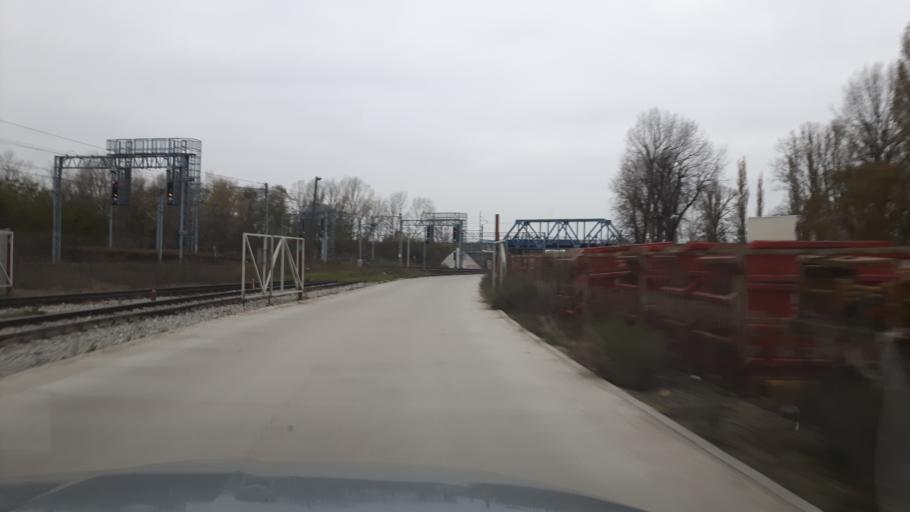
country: PL
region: Masovian Voivodeship
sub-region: Warszawa
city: Praga Polnoc
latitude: 52.2694
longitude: 21.0293
